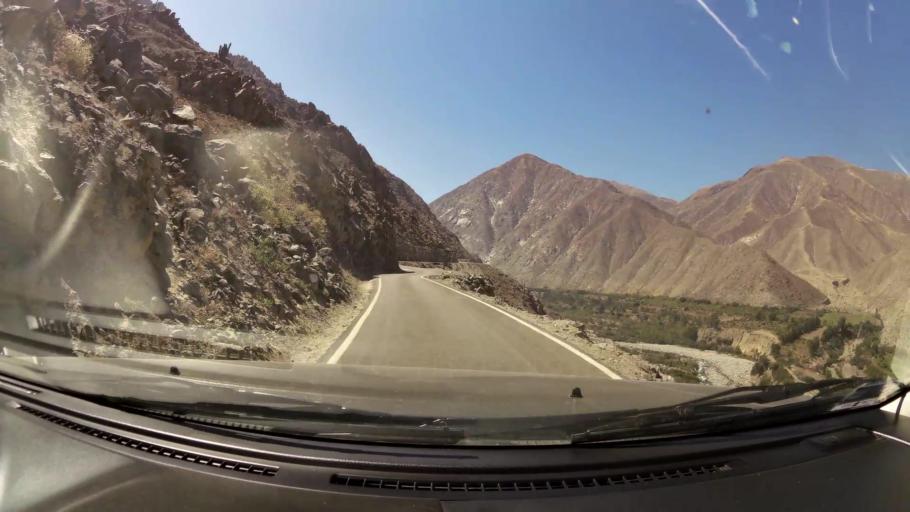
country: PE
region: Ica
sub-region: Provincia de Pisco
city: Huancano
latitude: -13.8347
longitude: -75.5508
